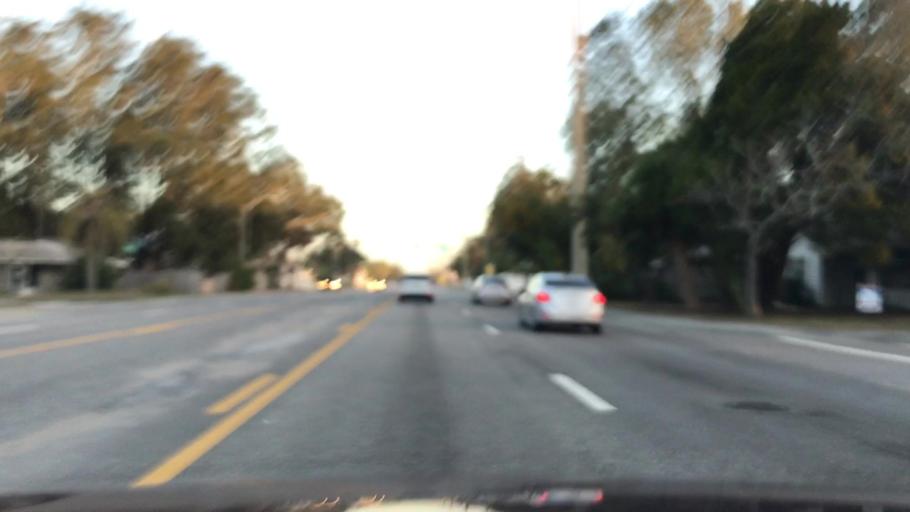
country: US
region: Florida
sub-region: Sarasota County
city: Sarasota
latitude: 27.3325
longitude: -82.5140
